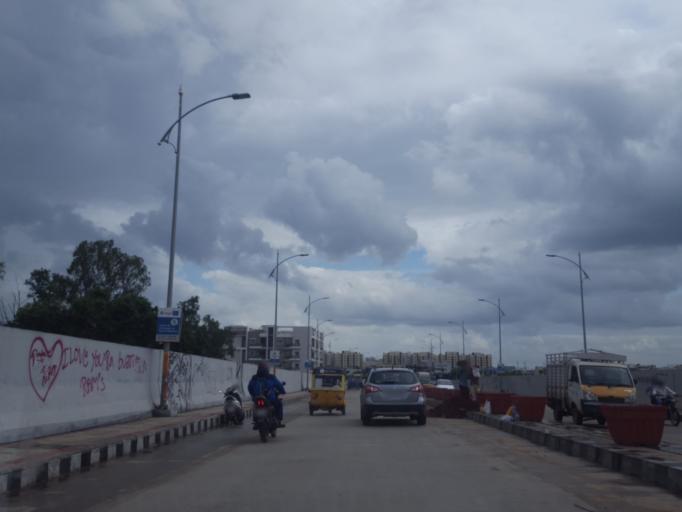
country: IN
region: Telangana
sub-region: Medak
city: Serilingampalle
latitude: 17.4818
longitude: 78.3112
